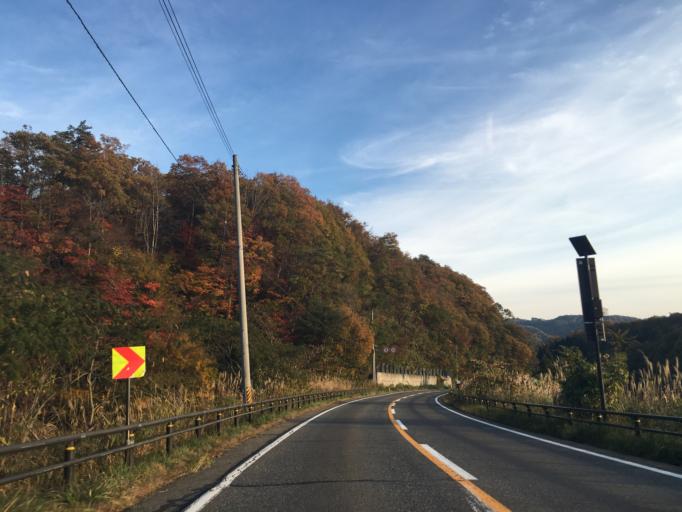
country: JP
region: Fukushima
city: Kitakata
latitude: 37.5615
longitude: 139.7353
